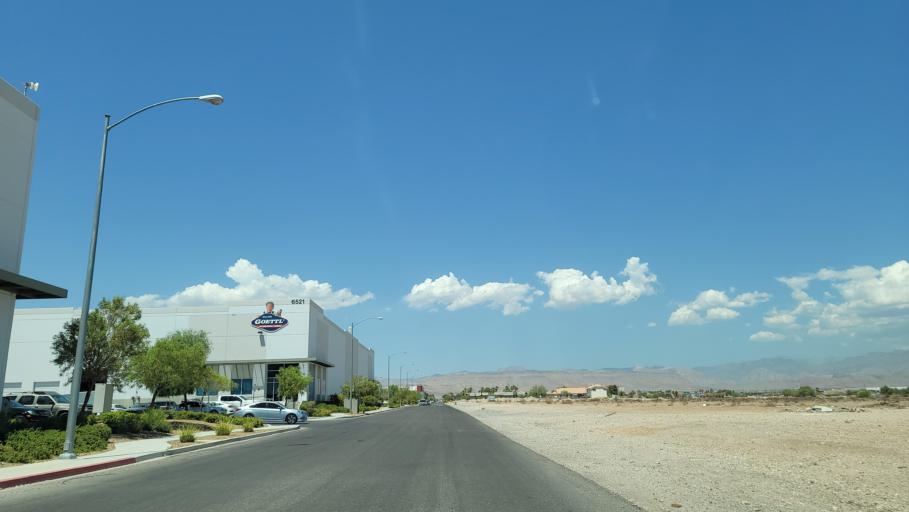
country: US
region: Nevada
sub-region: Clark County
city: Spring Valley
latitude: 36.0744
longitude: -115.2330
